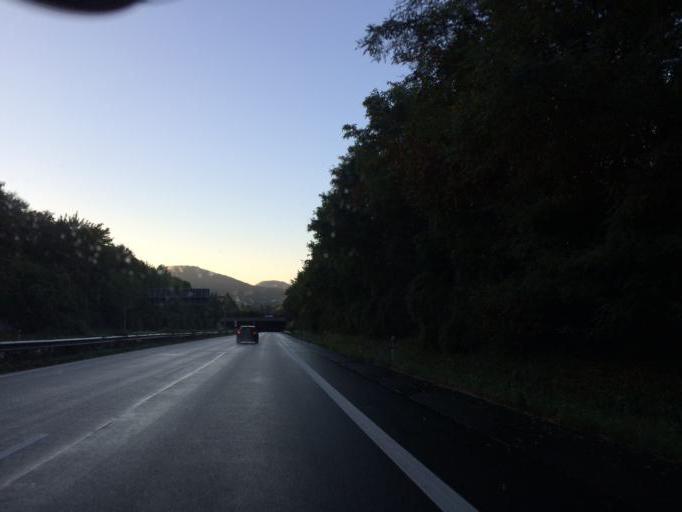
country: DE
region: North Rhine-Westphalia
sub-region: Regierungsbezirk Koln
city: Konigswinter
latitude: 50.7154
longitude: 7.1726
